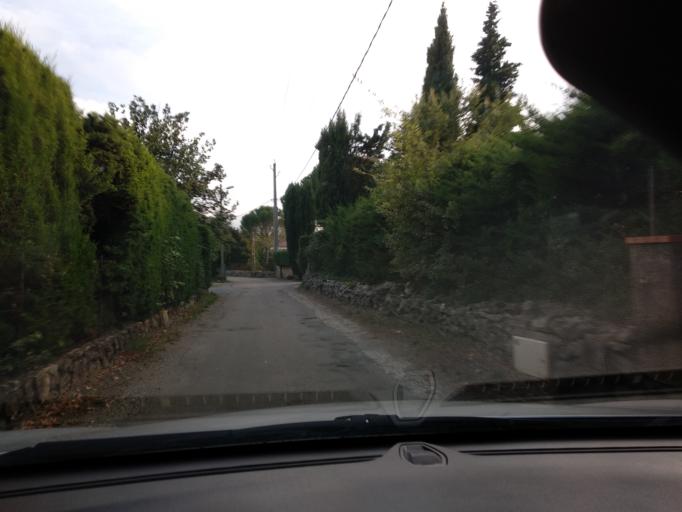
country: FR
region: Provence-Alpes-Cote d'Azur
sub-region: Departement des Alpes-Maritimes
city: Saint-Cezaire-sur-Siagne
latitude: 43.6562
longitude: 6.8018
